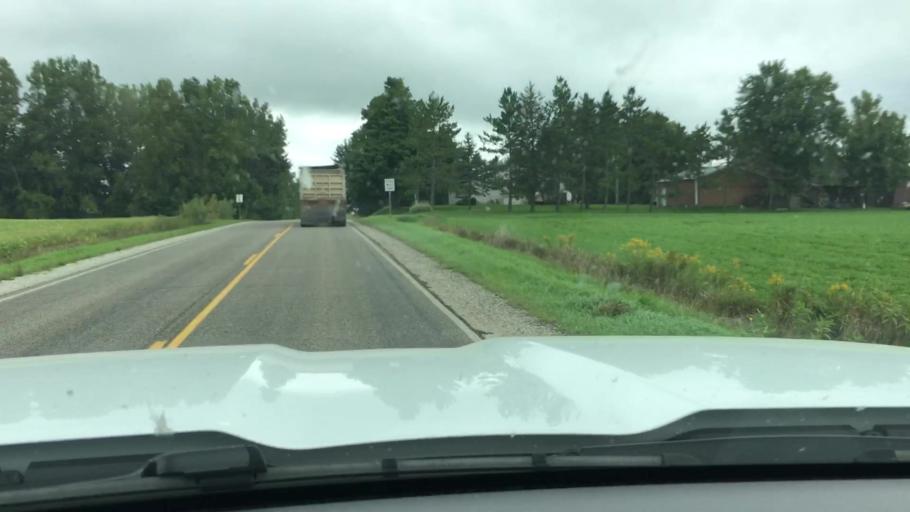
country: US
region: Michigan
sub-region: Montcalm County
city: Carson City
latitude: 43.2363
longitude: -84.7775
